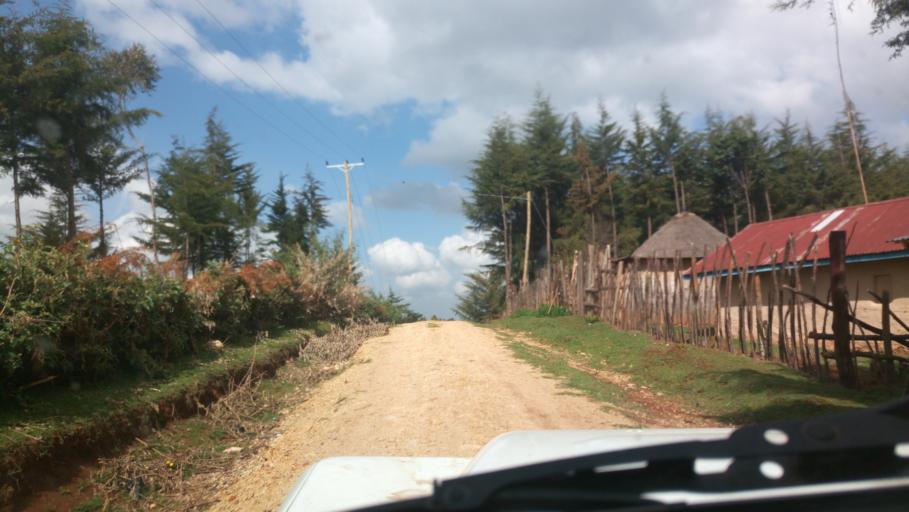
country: KE
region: Nakuru
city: Molo
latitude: -0.4592
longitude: 35.6710
